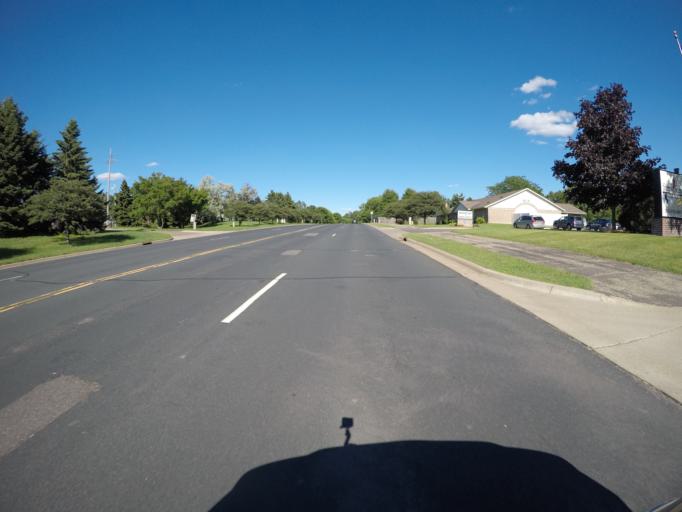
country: US
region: Minnesota
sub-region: Hennepin County
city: Maple Grove
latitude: 45.0873
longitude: -93.4274
